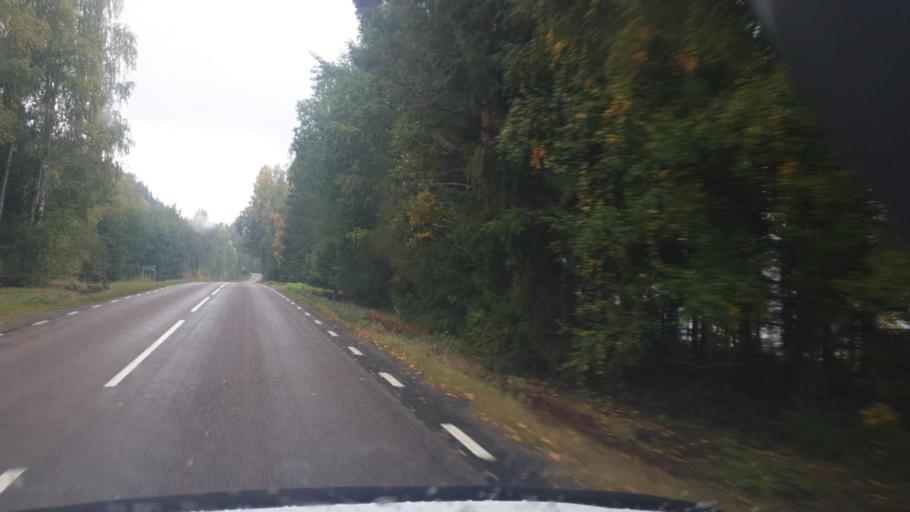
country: SE
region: Vaermland
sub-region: Sunne Kommun
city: Sunne
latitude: 59.8148
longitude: 13.0171
